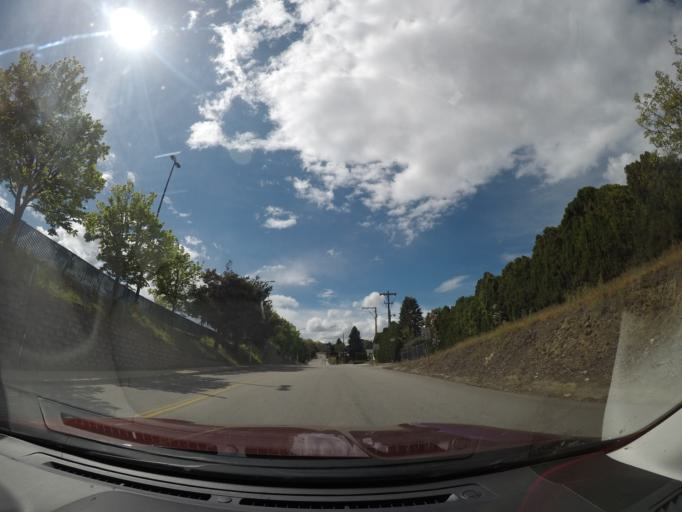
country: US
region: Washington
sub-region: Chelan County
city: Sunnyslope
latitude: 47.4551
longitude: -120.3368
